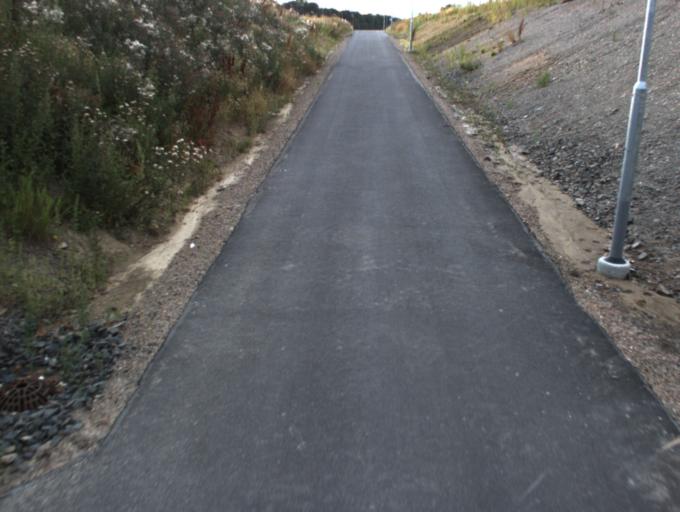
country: SE
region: Skane
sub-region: Helsingborg
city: Odakra
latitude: 56.0642
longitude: 12.7466
